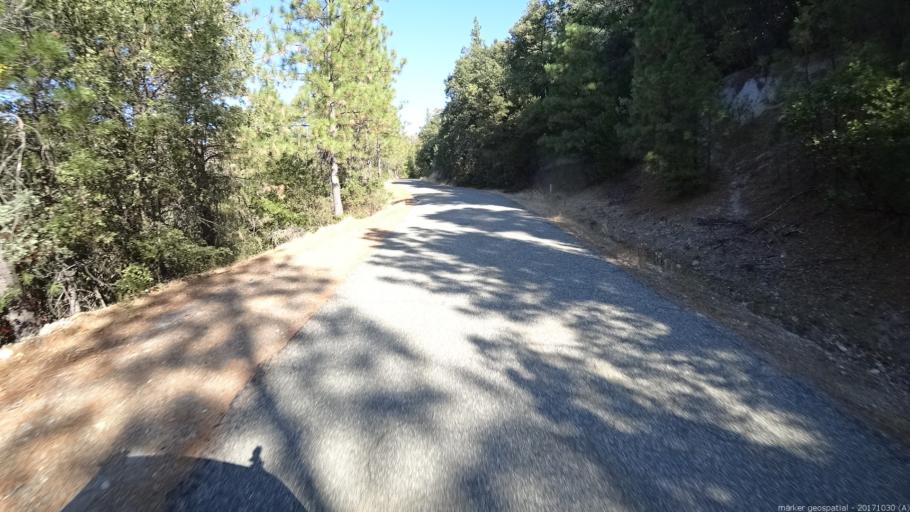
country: US
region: California
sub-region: Shasta County
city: Shingletown
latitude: 40.5793
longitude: -121.8770
